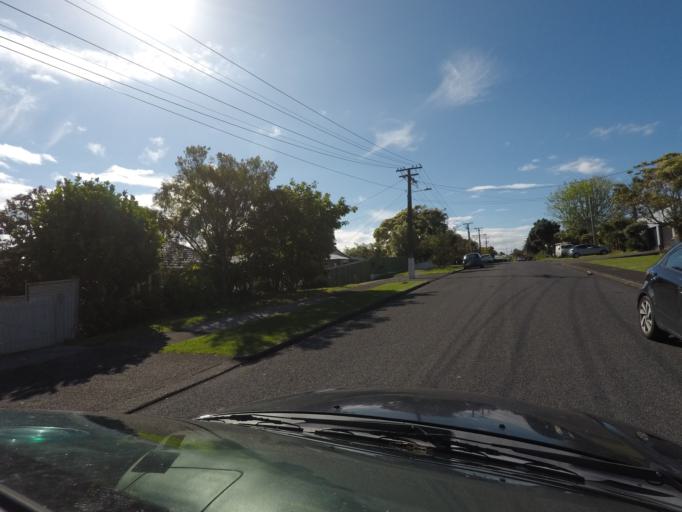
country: NZ
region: Auckland
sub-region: Auckland
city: Rosebank
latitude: -36.8625
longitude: 174.6548
